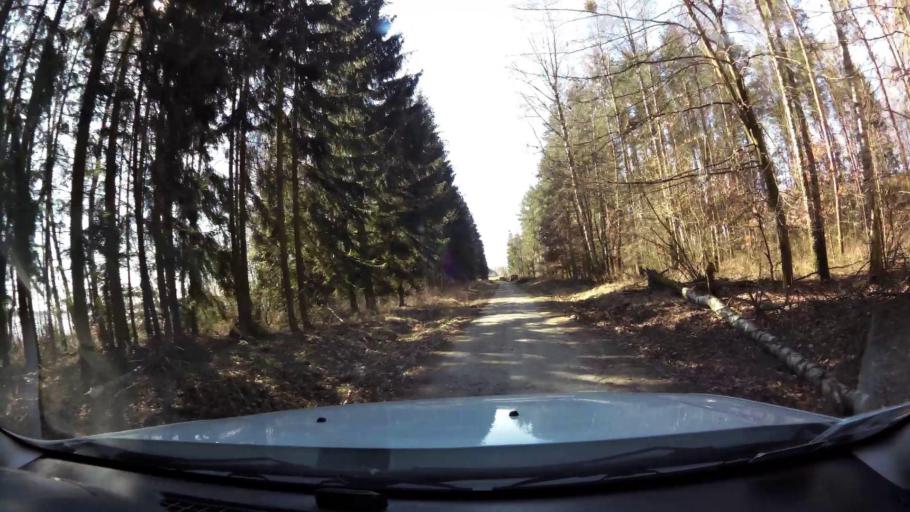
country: PL
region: West Pomeranian Voivodeship
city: Trzcinsko Zdroj
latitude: 52.9994
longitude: 14.6105
